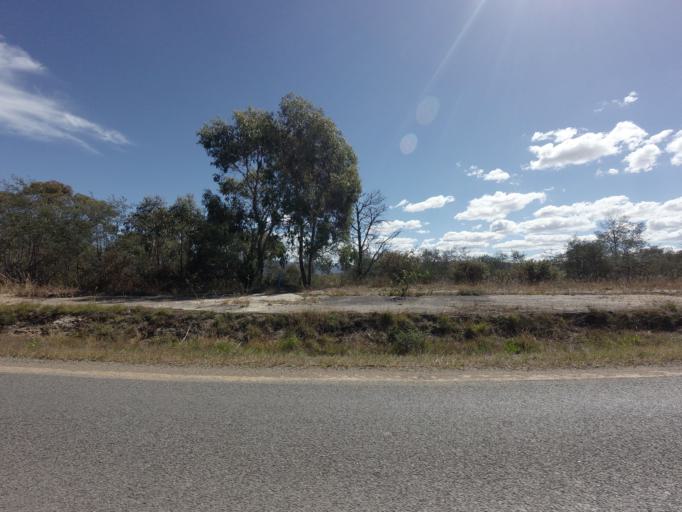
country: AU
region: Tasmania
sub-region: Break O'Day
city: St Helens
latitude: -41.6451
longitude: 147.9607
